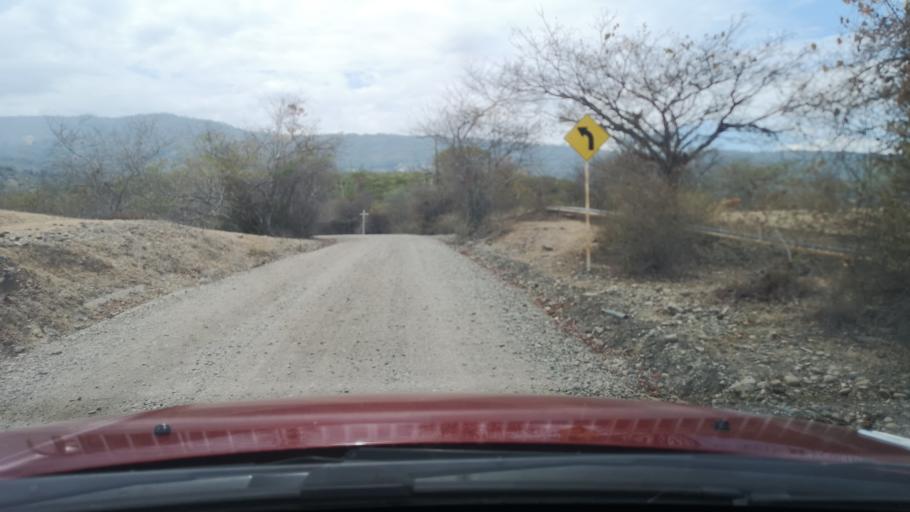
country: CO
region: Huila
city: Neiva
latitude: 2.9576
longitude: -75.3390
